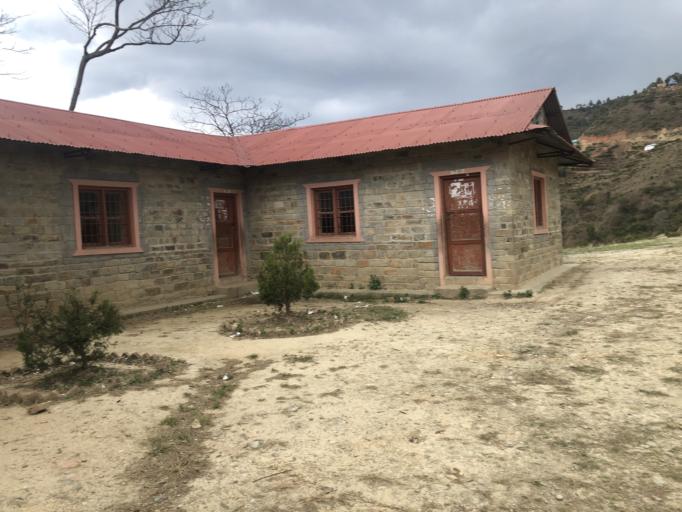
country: NP
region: Central Region
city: Banepa
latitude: 27.5571
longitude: 85.8021
